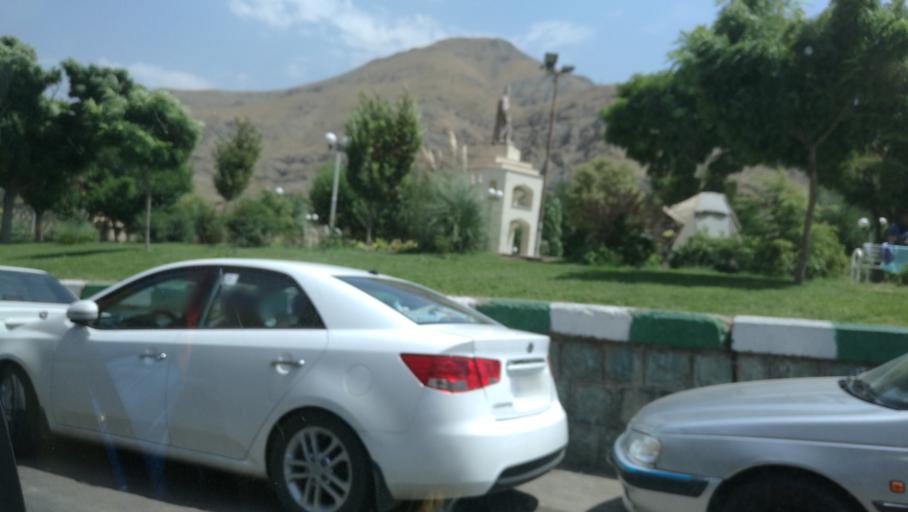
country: IR
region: Alborz
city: Karaj
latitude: 35.8358
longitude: 51.0447
